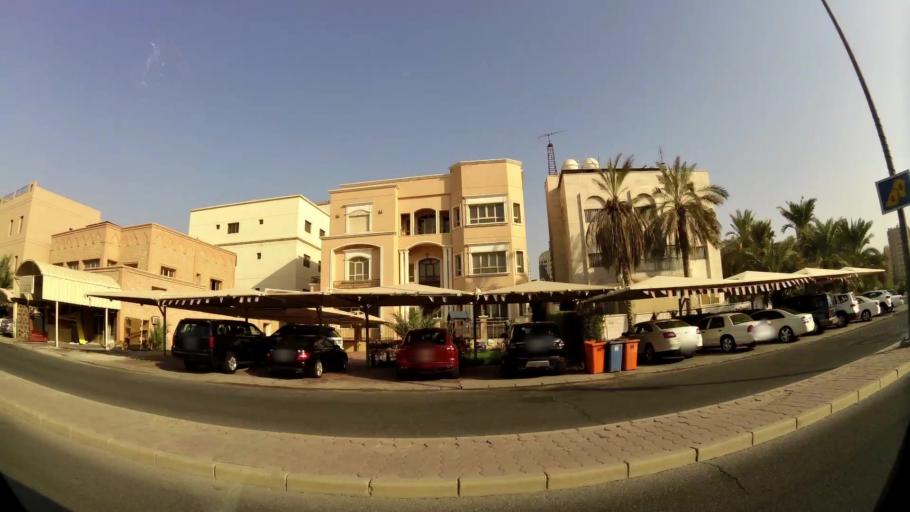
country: KW
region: Al Asimah
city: Ad Dasmah
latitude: 29.3658
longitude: 48.0052
